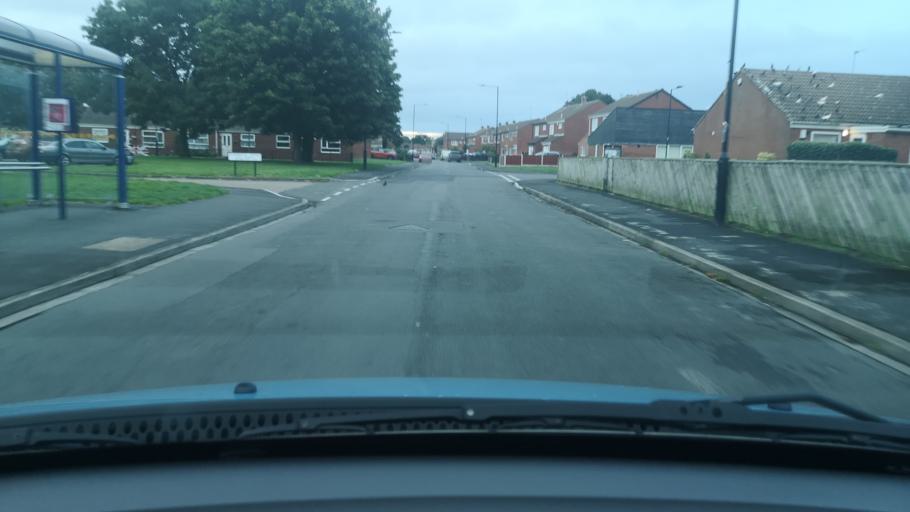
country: GB
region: England
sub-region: Doncaster
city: Askern
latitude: 53.6144
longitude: -1.1397
